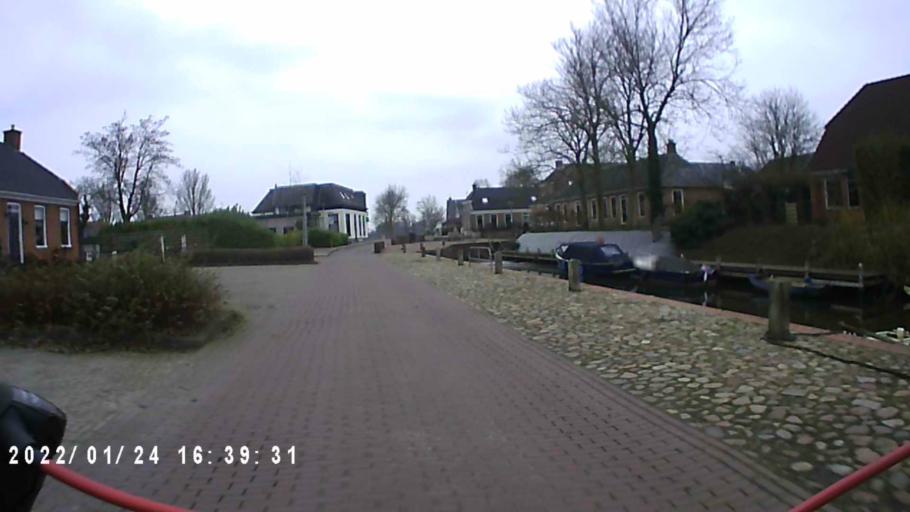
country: NL
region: Groningen
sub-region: Gemeente De Marne
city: Ulrum
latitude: 53.3864
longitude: 6.4042
